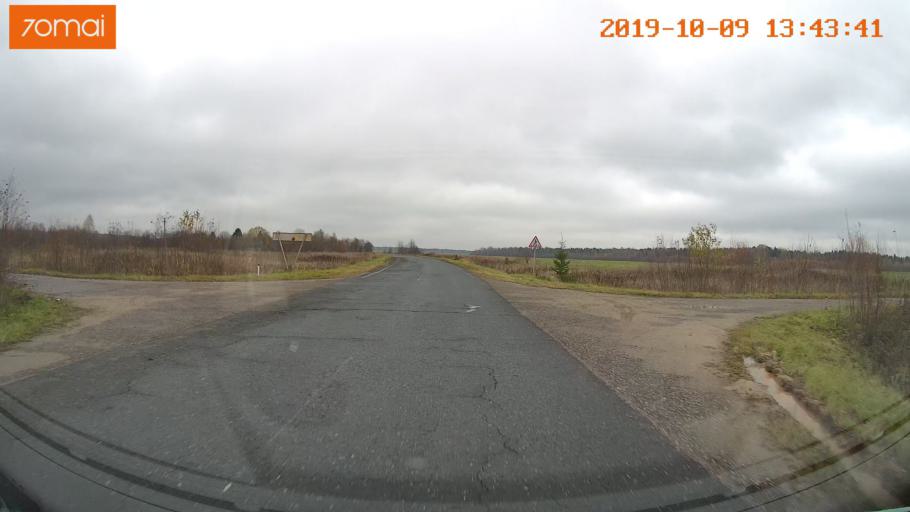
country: RU
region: Kostroma
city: Buy
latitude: 58.3589
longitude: 41.2029
